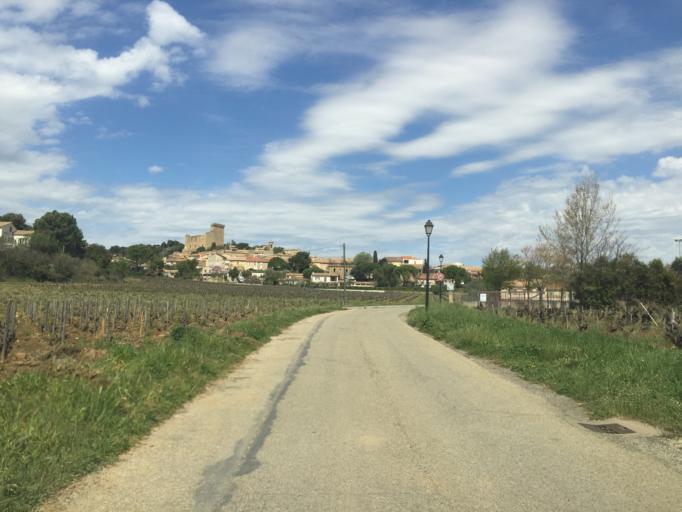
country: FR
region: Provence-Alpes-Cote d'Azur
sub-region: Departement du Vaucluse
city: Chateauneuf-du-Pape
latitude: 44.0520
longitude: 4.8313
